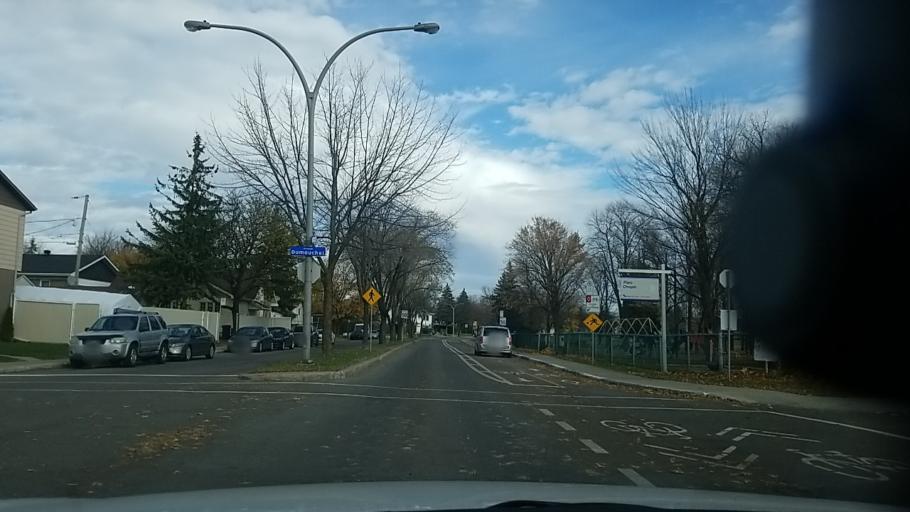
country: CA
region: Quebec
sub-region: Laval
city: Laval
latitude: 45.5708
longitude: -73.7373
